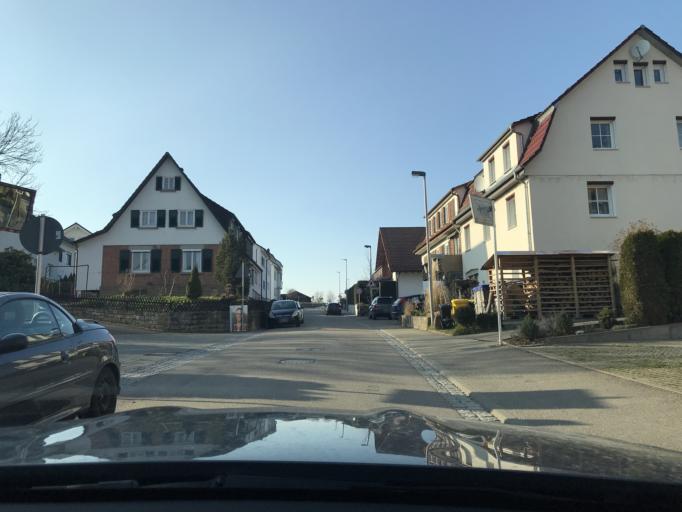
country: DE
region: Baden-Wuerttemberg
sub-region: Regierungsbezirk Stuttgart
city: Korb
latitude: 48.8294
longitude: 9.3725
